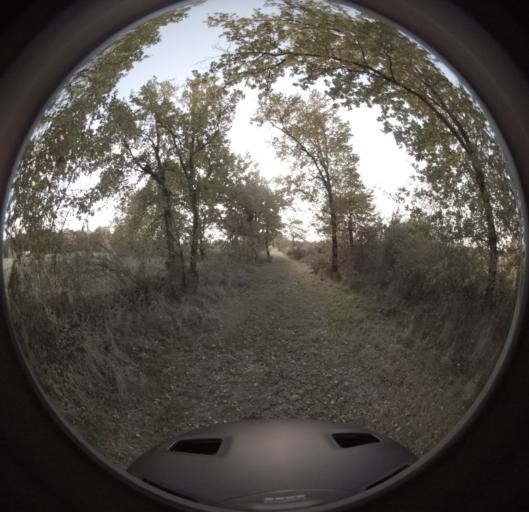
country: FR
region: Midi-Pyrenees
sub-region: Departement du Tarn-et-Garonne
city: Montbeton
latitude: 43.9888
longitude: 1.2858
